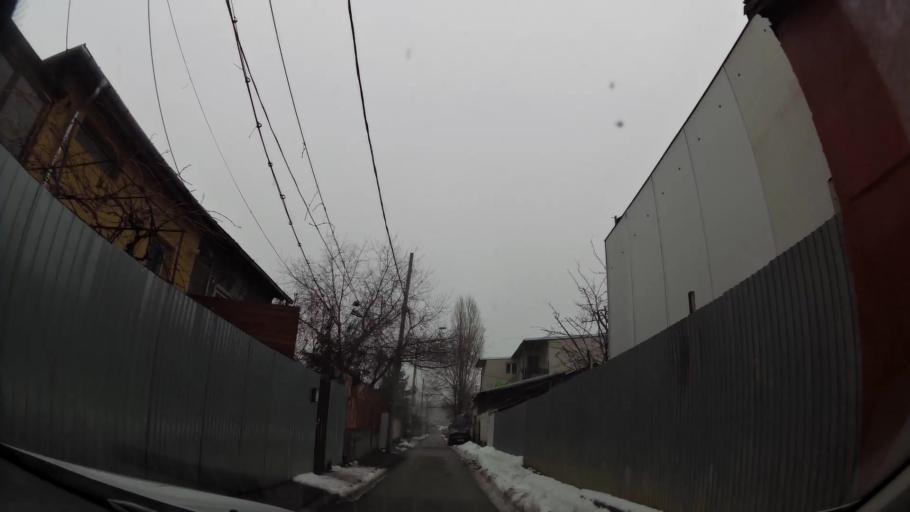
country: RO
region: Ilfov
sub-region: Comuna Chiajna
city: Rosu
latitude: 44.4602
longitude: 26.0499
